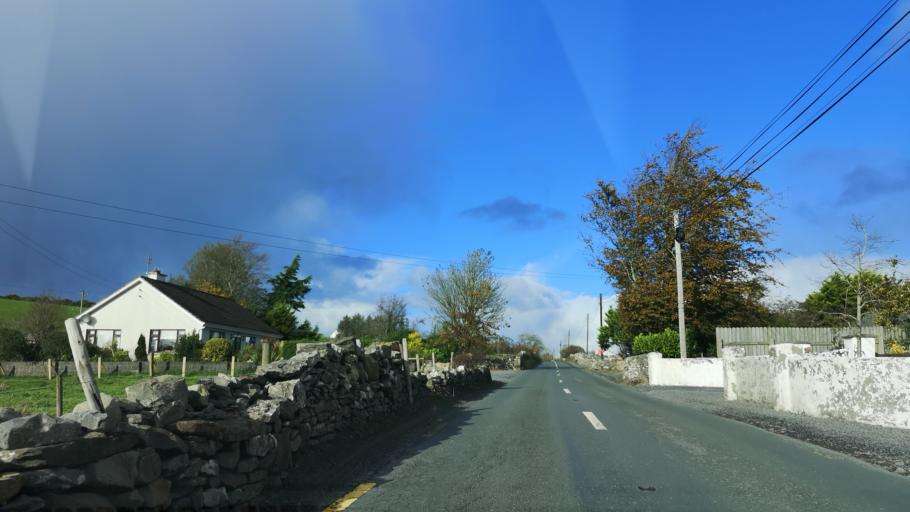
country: IE
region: Connaught
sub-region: Maigh Eo
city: Castlebar
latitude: 53.7680
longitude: -9.3832
